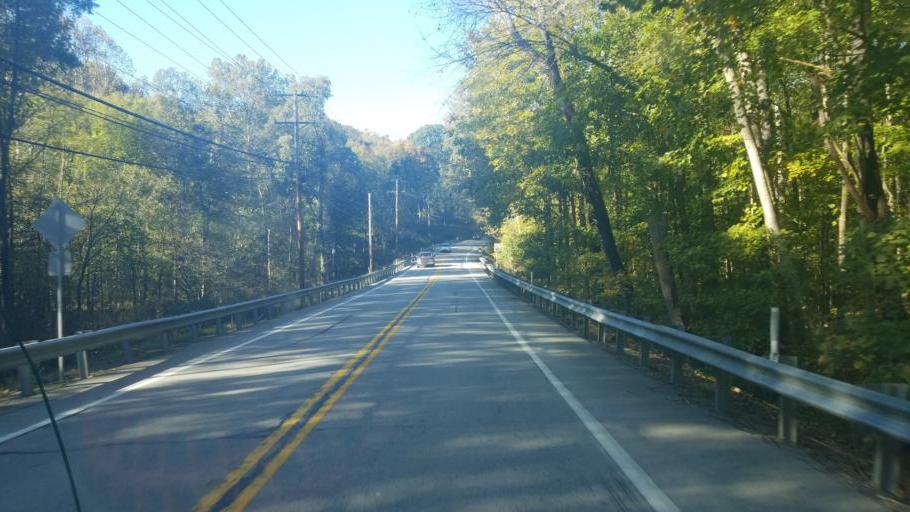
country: US
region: Pennsylvania
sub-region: Washington County
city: Burgettstown
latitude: 40.4995
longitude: -80.3635
